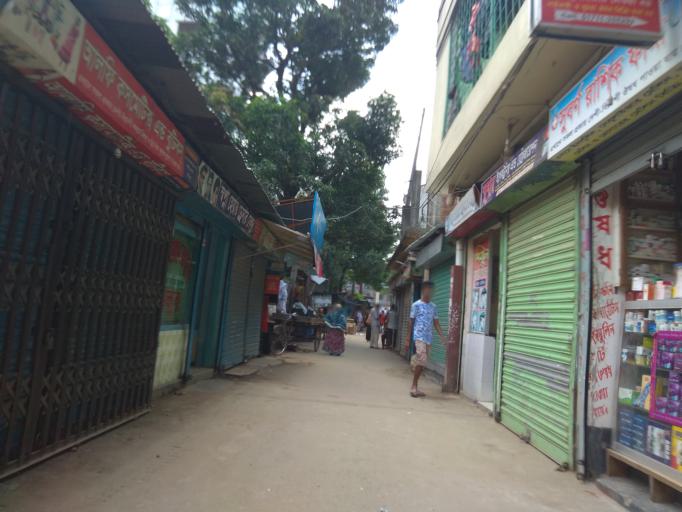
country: BD
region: Dhaka
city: Tungi
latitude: 23.8247
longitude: 90.3931
